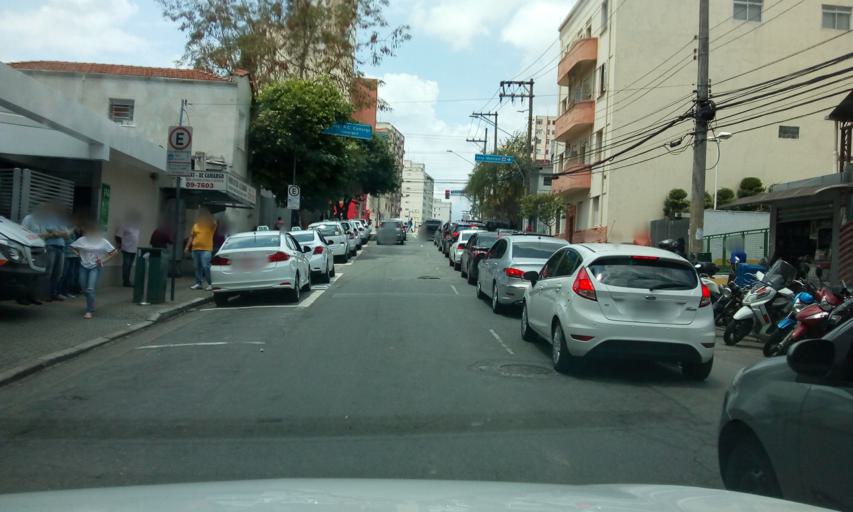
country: BR
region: Sao Paulo
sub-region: Sao Paulo
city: Sao Paulo
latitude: -23.5658
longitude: -46.6376
